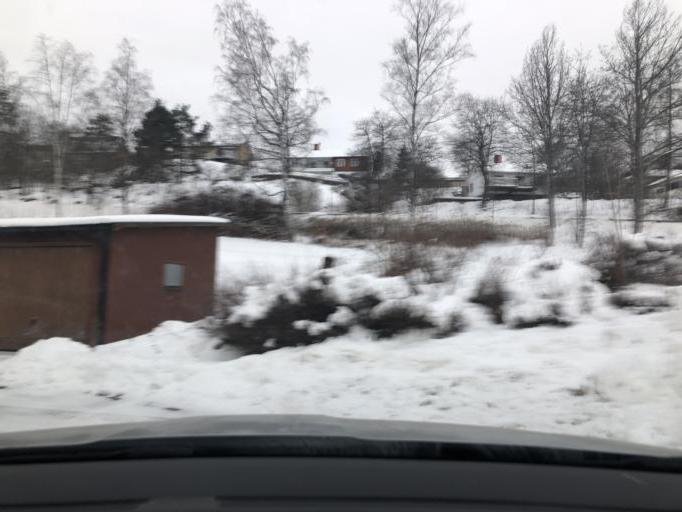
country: SE
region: OEstergoetland
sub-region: Kinda Kommun
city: Kisa
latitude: 57.9842
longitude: 15.6321
